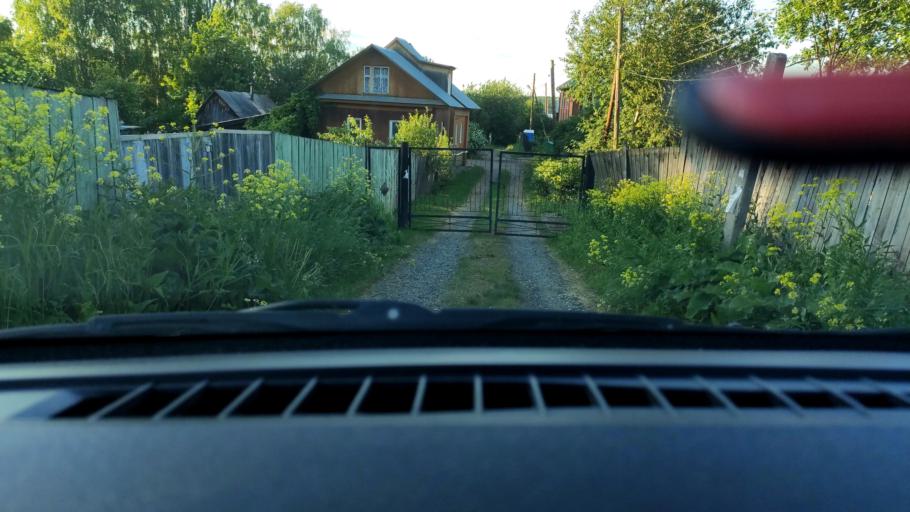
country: RU
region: Perm
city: Kultayevo
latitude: 57.9367
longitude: 55.8626
